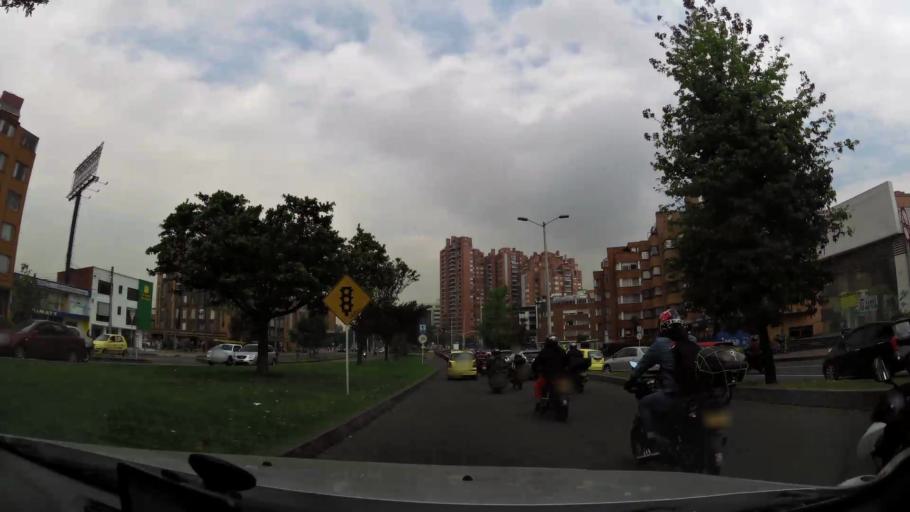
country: CO
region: Bogota D.C.
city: Barrio San Luis
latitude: 4.6897
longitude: -74.0675
